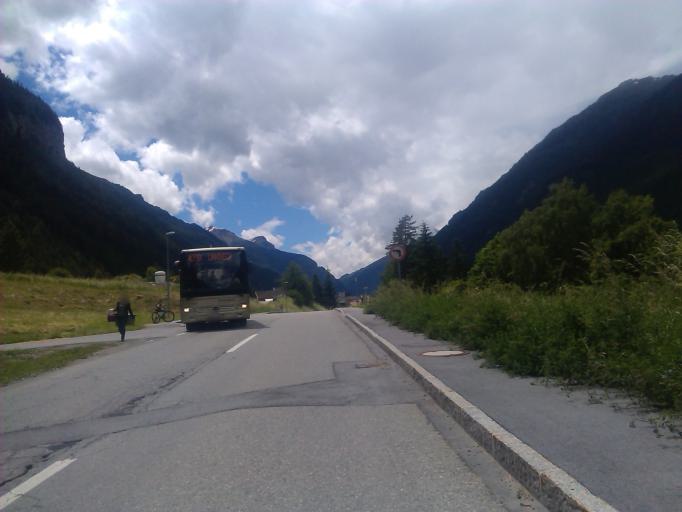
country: AT
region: Tyrol
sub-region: Politischer Bezirk Landeck
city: Serfaus
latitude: 47.0254
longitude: 10.6214
